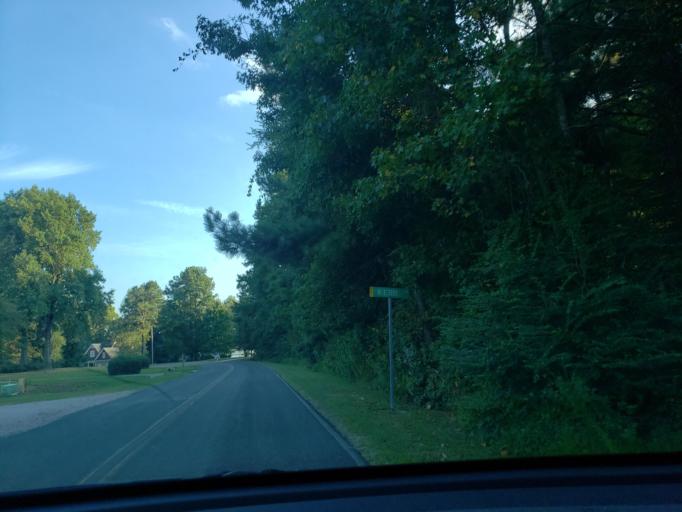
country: US
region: North Carolina
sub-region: Vance County
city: Henderson
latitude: 36.4026
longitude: -78.3747
